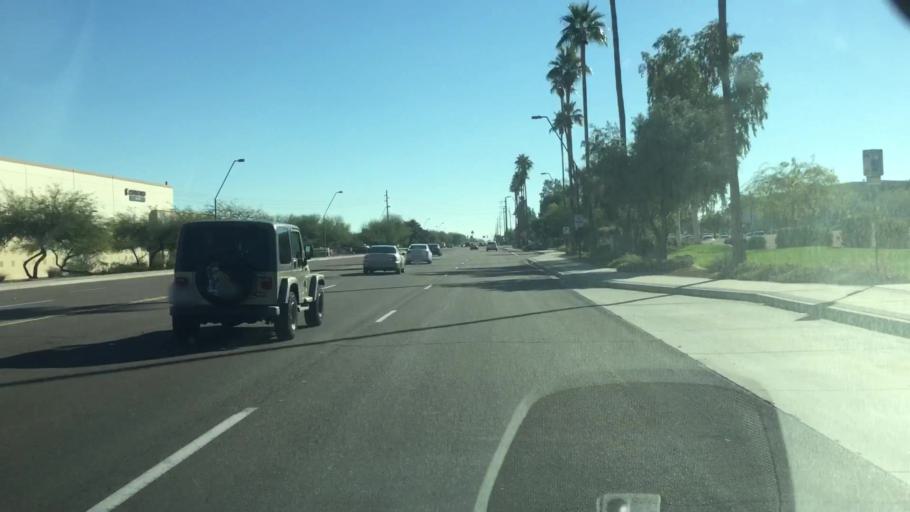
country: US
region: Arizona
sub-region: Maricopa County
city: Guadalupe
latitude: 33.3397
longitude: -111.9632
